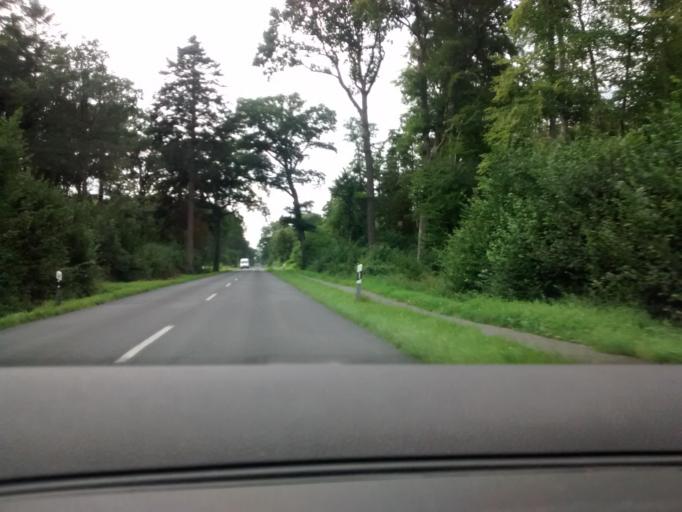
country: DE
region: Lower Saxony
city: Brietlingen
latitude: 53.3194
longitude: 10.4766
